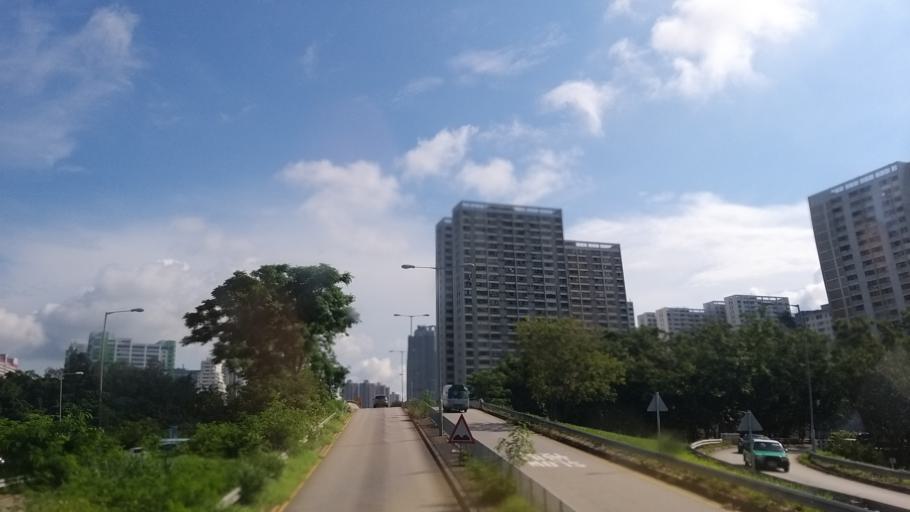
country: HK
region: Tuen Mun
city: Tuen Mun
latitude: 22.3851
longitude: 113.9708
